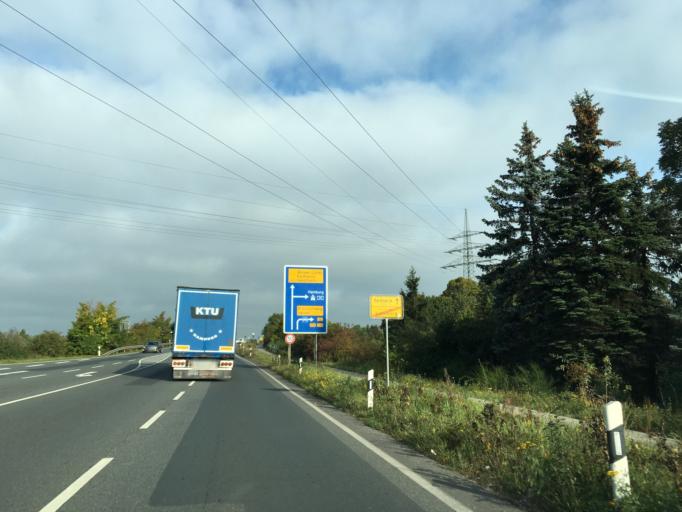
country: DE
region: Lower Saxony
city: Bardowick
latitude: 53.2752
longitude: 10.4021
